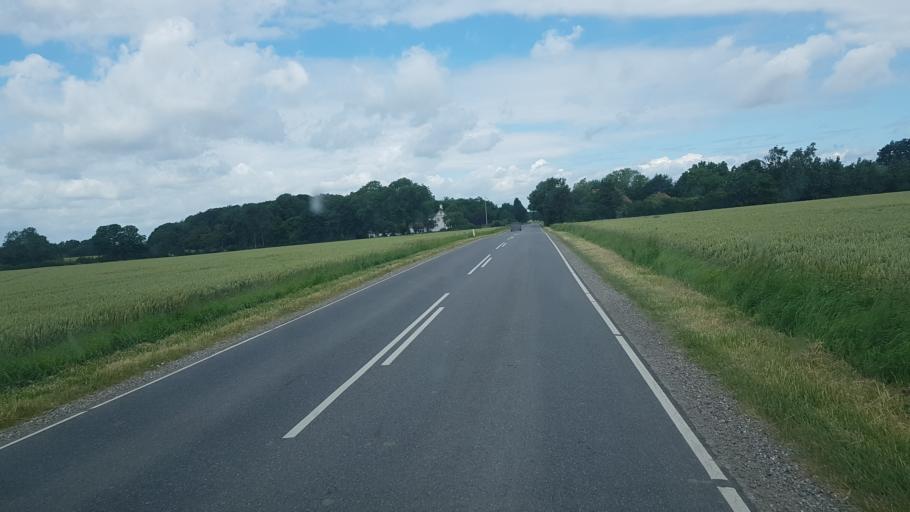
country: DK
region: South Denmark
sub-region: Kerteminde Kommune
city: Kerteminde
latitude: 55.4065
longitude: 10.7228
